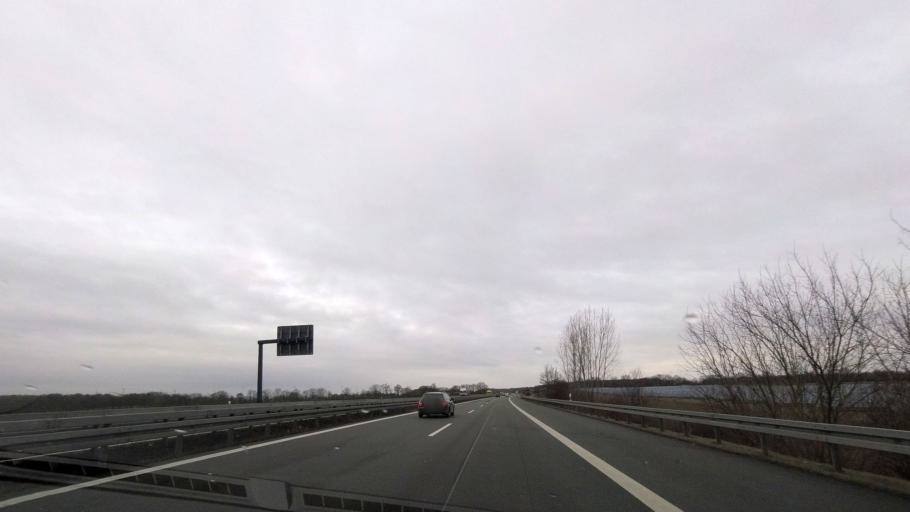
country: DE
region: Brandenburg
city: Gerdshagen
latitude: 53.2417
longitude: 12.1867
